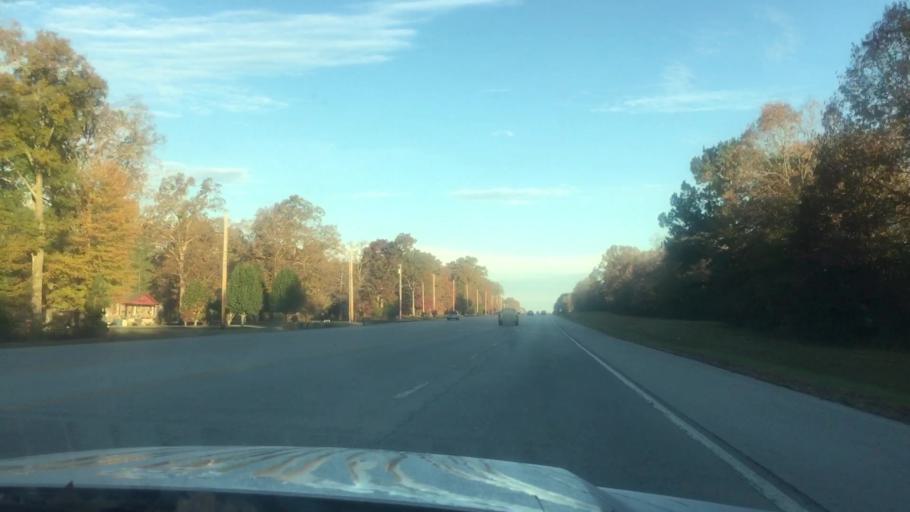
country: US
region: Tennessee
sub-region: Franklin County
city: Estill Springs
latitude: 35.3163
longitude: -86.1683
